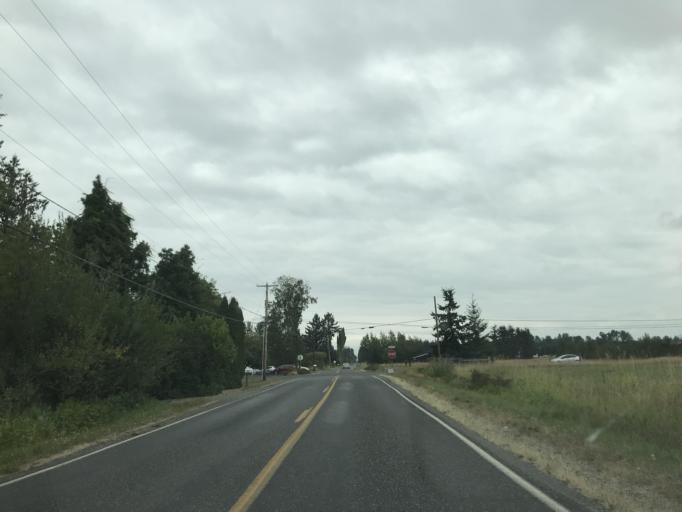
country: US
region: Washington
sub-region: Whatcom County
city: Everson
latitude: 48.8318
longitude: -122.3325
